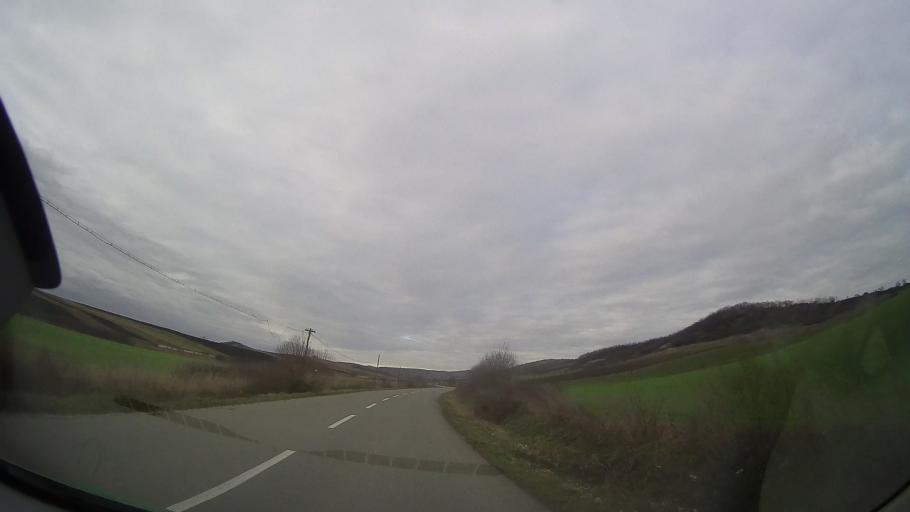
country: RO
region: Bistrita-Nasaud
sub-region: Comuna Milas
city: Milas
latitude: 46.7991
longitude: 24.4238
